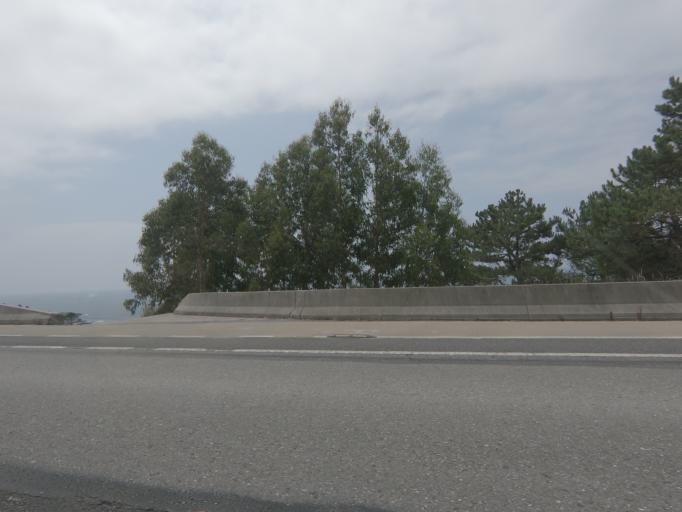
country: ES
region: Galicia
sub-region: Provincia de Pontevedra
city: Oia
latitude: 41.9768
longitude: -8.8847
